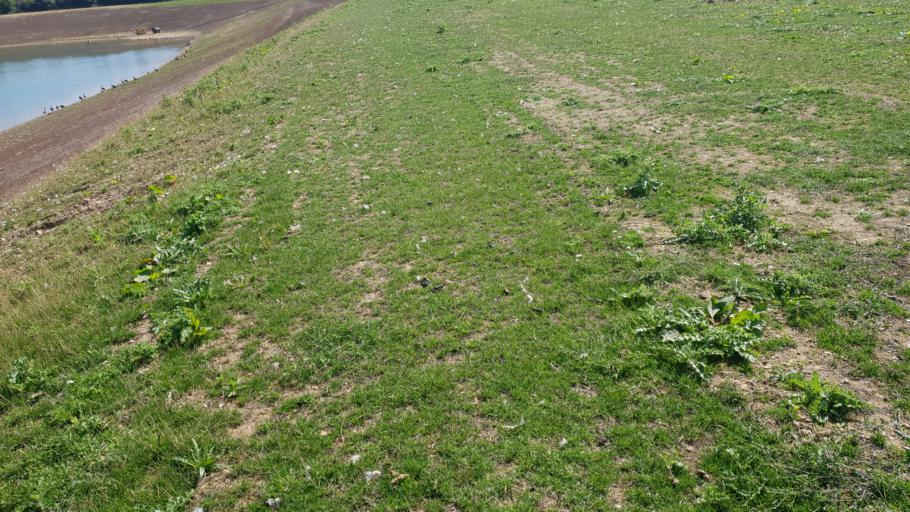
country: GB
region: England
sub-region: Essex
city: Colchester
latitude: 51.9223
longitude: 0.9537
